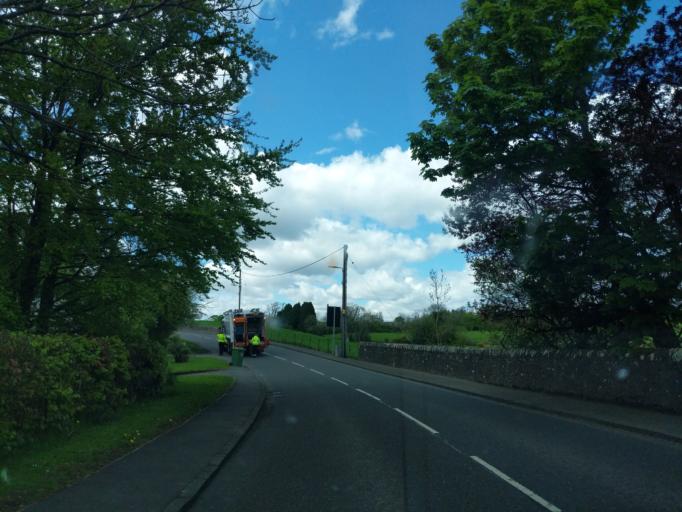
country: GB
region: Scotland
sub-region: Stirling
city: Doune
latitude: 56.1739
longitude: -4.1396
